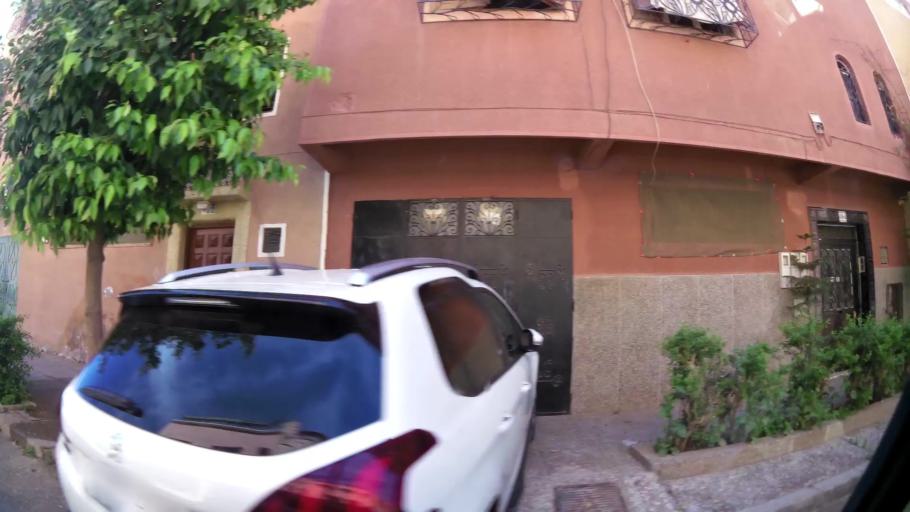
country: MA
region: Marrakech-Tensift-Al Haouz
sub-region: Marrakech
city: Marrakesh
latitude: 31.6586
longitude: -7.9863
